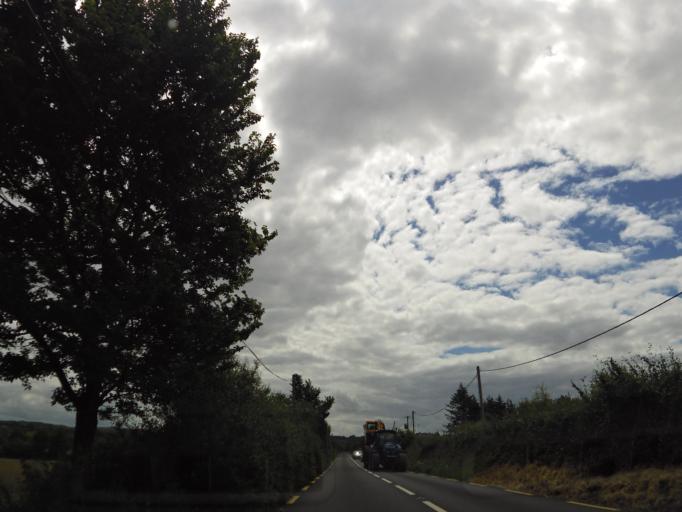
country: IE
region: Munster
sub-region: North Tipperary
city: Nenagh
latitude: 52.7851
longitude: -8.0343
